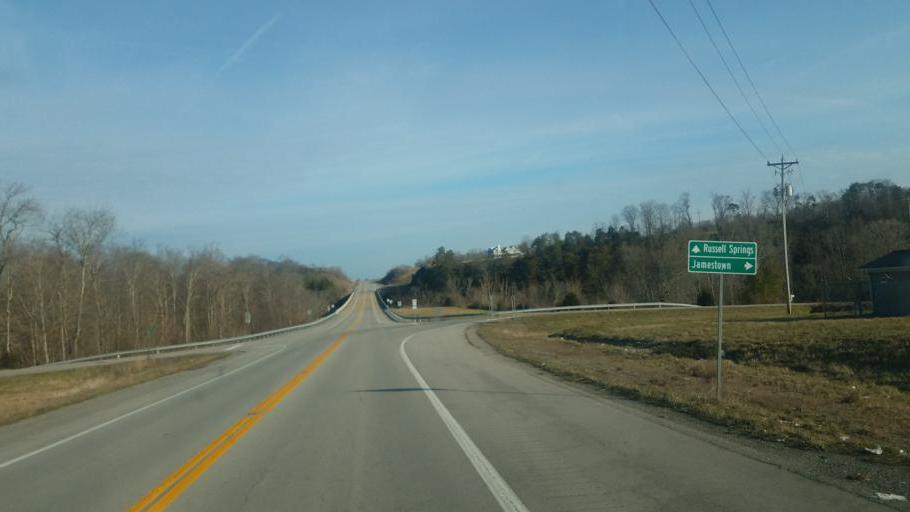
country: US
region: Kentucky
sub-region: Russell County
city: Jamestown
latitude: 36.9660
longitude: -85.0880
